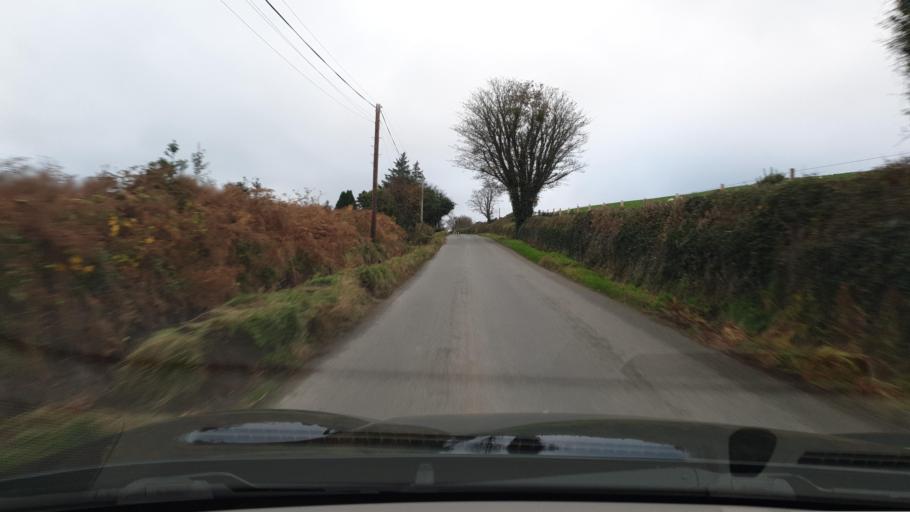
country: IE
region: Leinster
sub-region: Wicklow
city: Enniskerry
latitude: 53.1665
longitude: -6.1791
